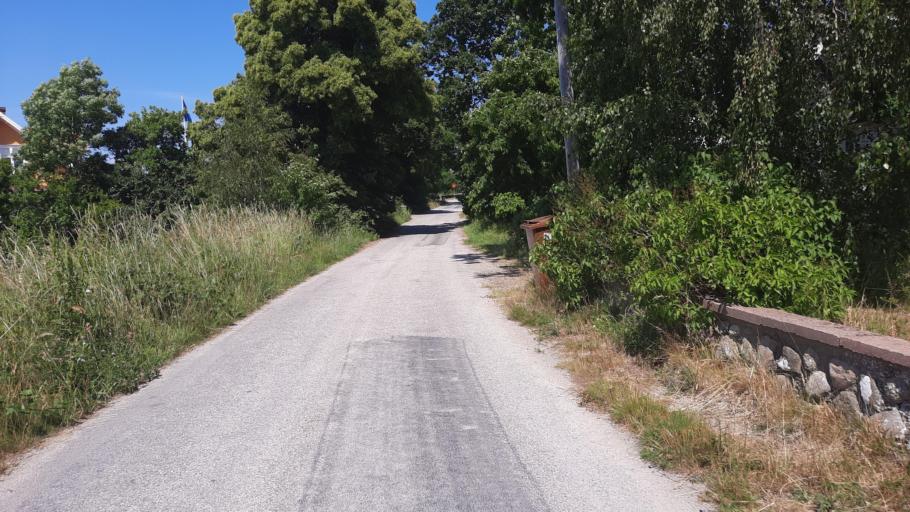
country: SE
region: Blekinge
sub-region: Karlskrona Kommun
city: Jaemjoe
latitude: 56.1469
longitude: 15.7716
